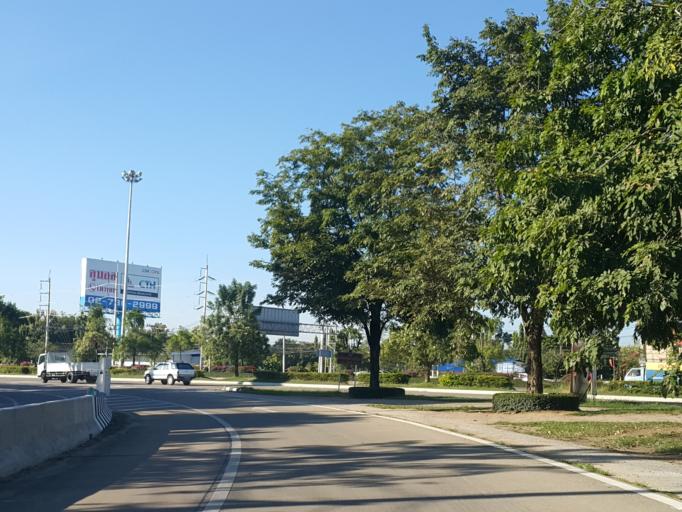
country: TH
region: Chiang Mai
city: Saraphi
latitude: 18.7643
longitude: 99.0301
